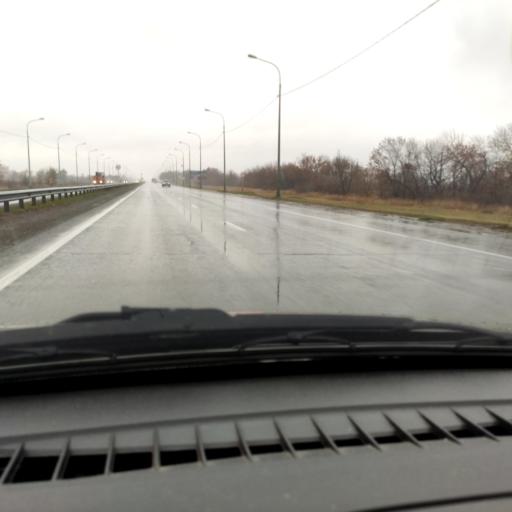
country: RU
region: Samara
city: Tol'yatti
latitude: 53.5732
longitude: 49.4572
